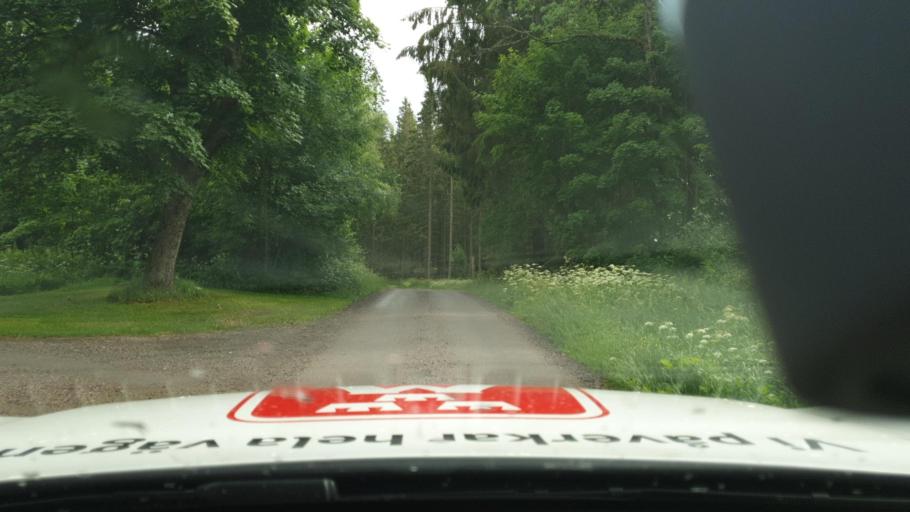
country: SE
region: Vaestra Goetaland
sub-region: Falkopings Kommun
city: Falkoeping
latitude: 58.0535
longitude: 13.6631
